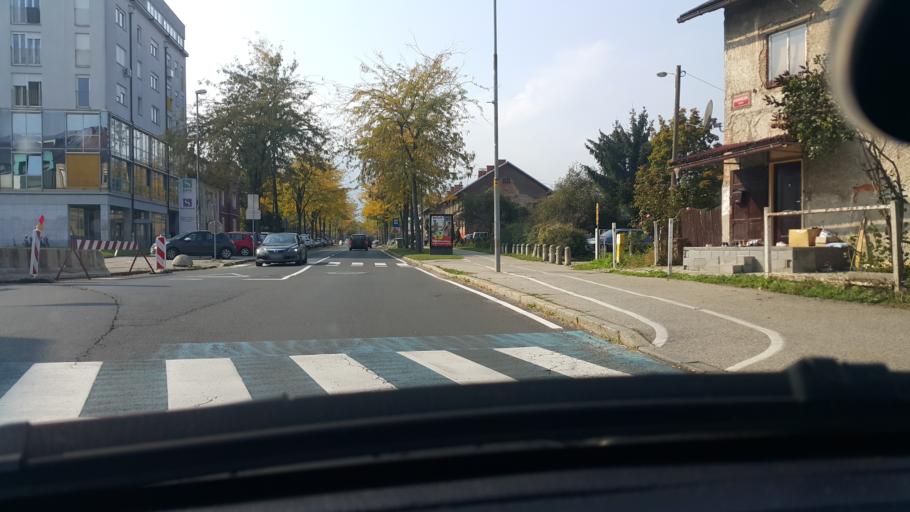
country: SI
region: Maribor
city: Maribor
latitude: 46.5517
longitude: 15.6408
